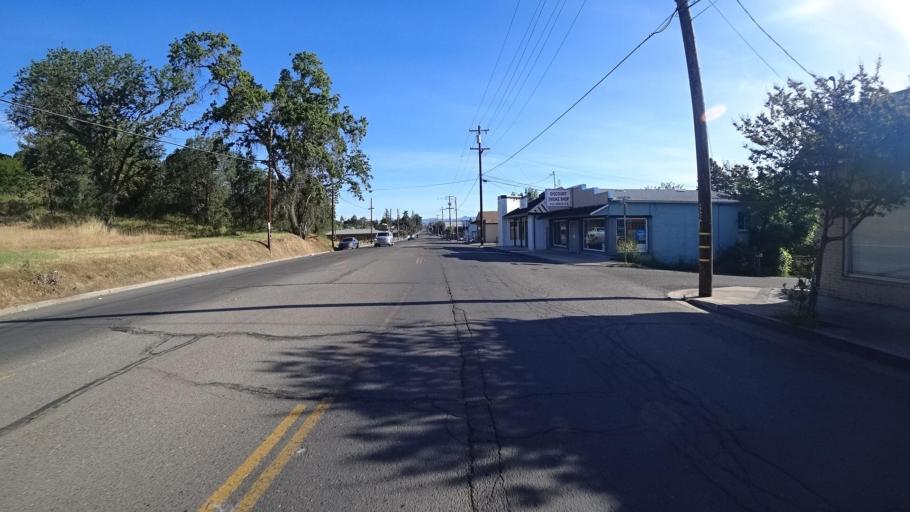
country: US
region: California
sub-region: Lake County
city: Lakeport
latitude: 39.0368
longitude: -122.9153
